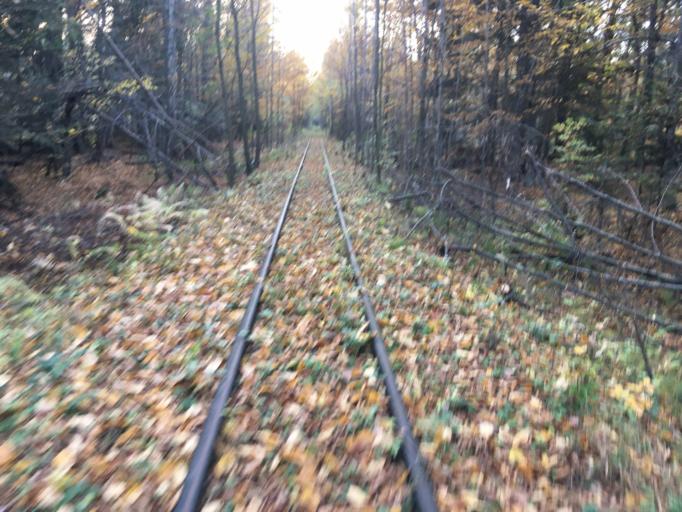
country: PL
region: Swietokrzyskie
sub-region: Powiat starachowicki
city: Brody
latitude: 51.0749
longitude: 21.1605
